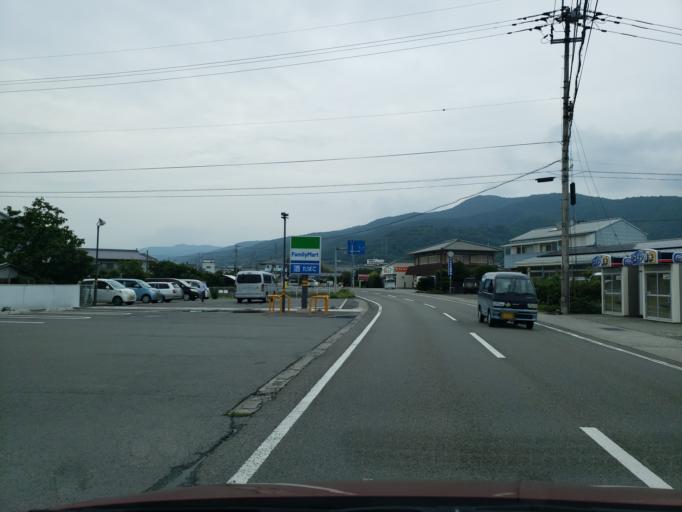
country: JP
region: Tokushima
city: Kamojimacho-jogejima
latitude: 34.1037
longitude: 134.2734
